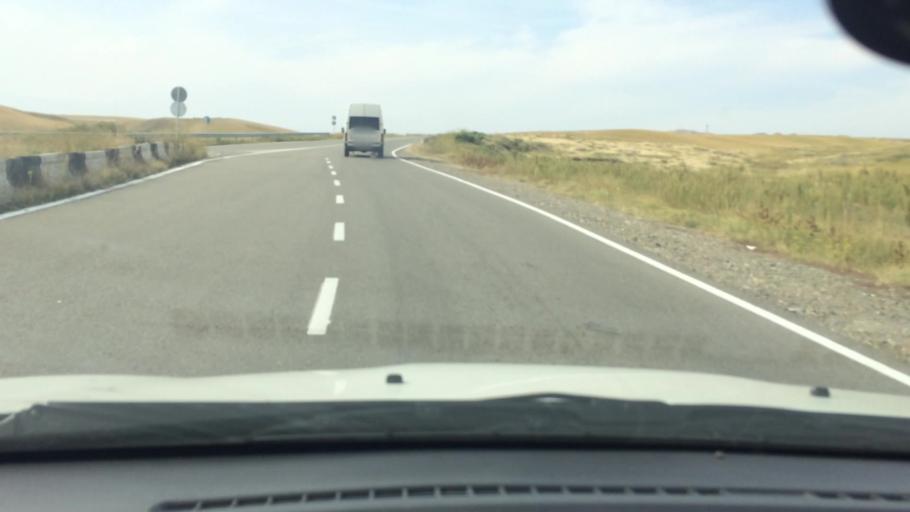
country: GE
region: Kvemo Kartli
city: Rust'avi
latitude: 41.5221
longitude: 44.9863
